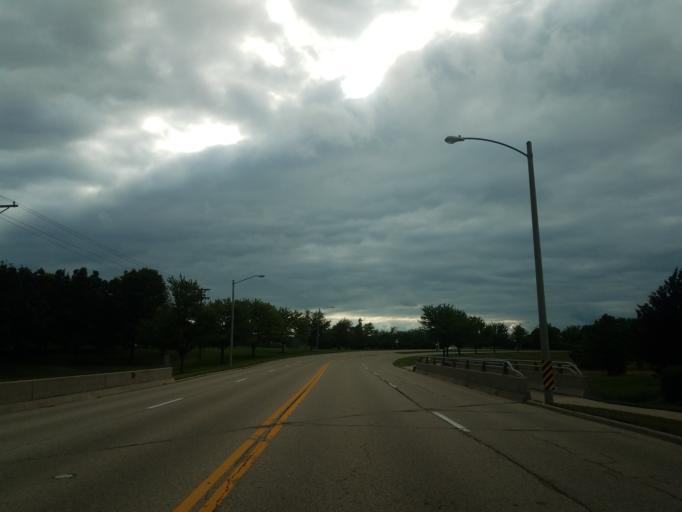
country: US
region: Illinois
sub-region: McLean County
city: Bloomington
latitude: 40.4592
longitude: -88.9475
